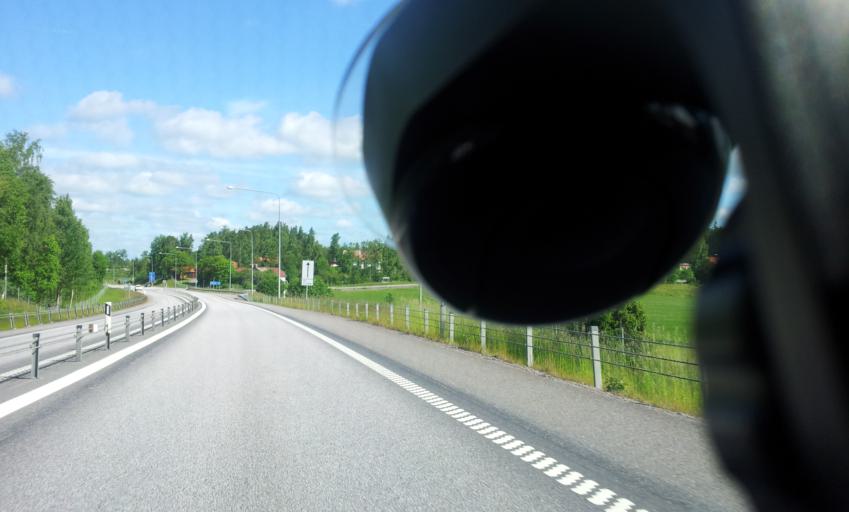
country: SE
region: OEstergoetland
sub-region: Soderkopings Kommun
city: Soederkoeping
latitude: 58.3952
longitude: 16.4103
